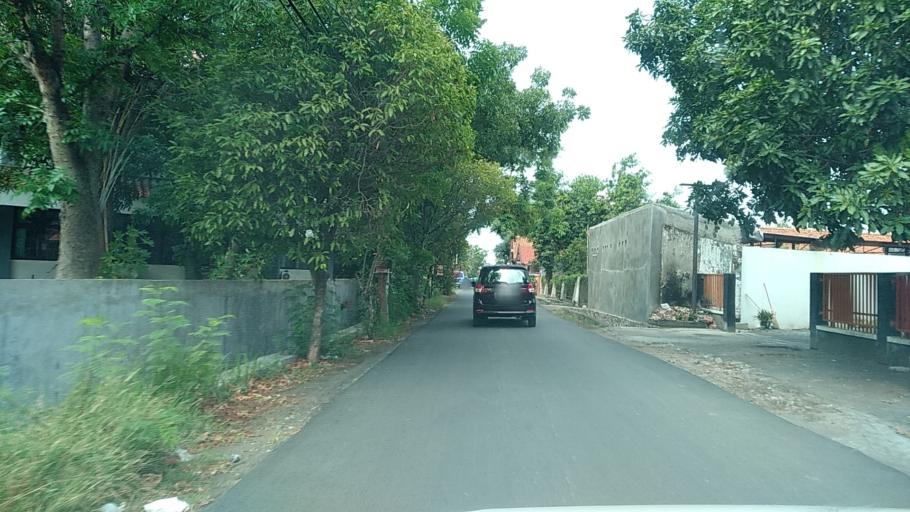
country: ID
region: Central Java
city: Semarang
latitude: -7.0004
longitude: 110.4492
